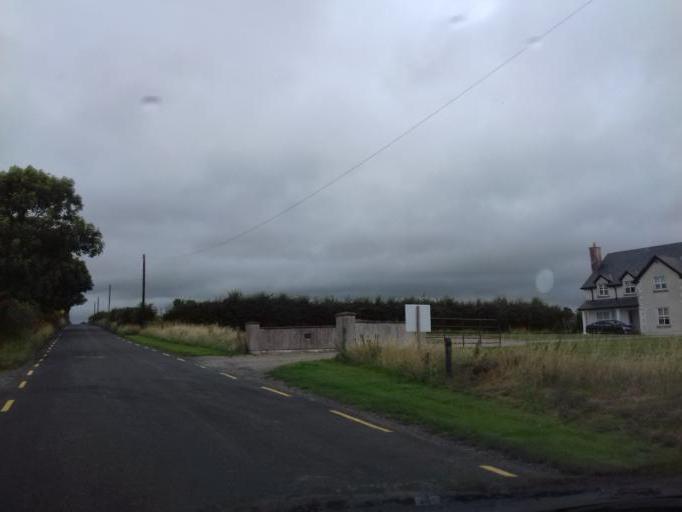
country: IE
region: Leinster
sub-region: Kilkenny
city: Graiguenamanagh
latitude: 52.6116
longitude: -7.0307
